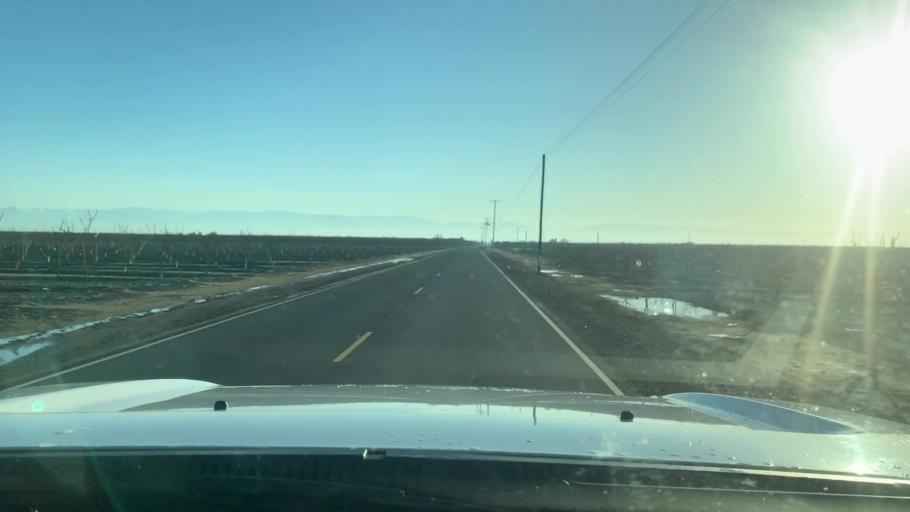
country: US
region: California
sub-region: Tulare County
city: Tulare
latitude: 36.2031
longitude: -119.4622
